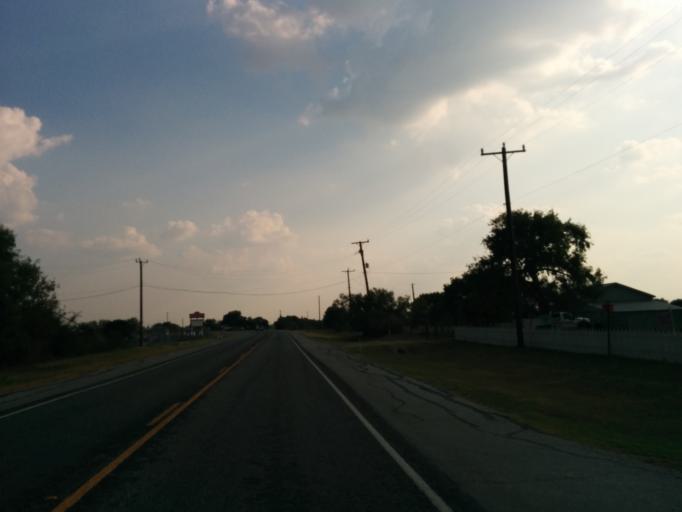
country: US
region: Texas
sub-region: Bexar County
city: Saint Hedwig
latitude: 29.4207
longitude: -98.2319
